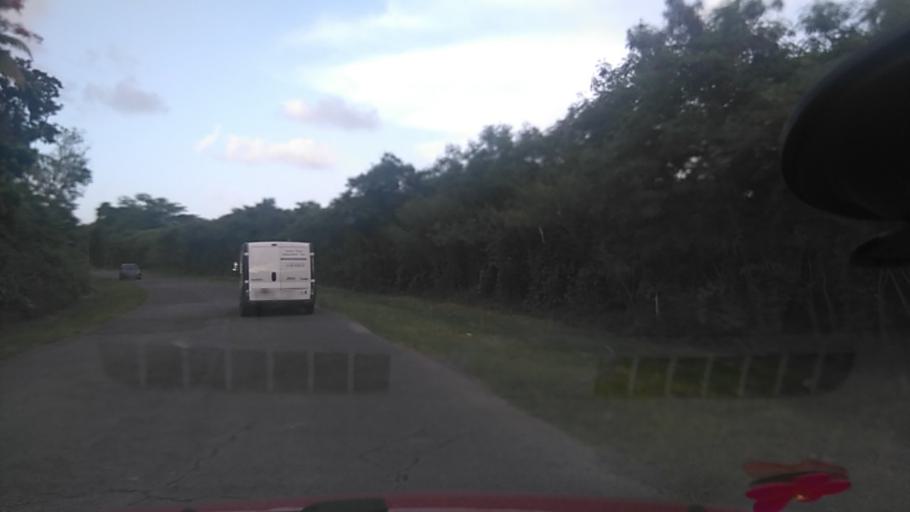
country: MQ
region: Martinique
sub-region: Martinique
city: Le Marin
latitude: 14.4669
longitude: -60.8638
